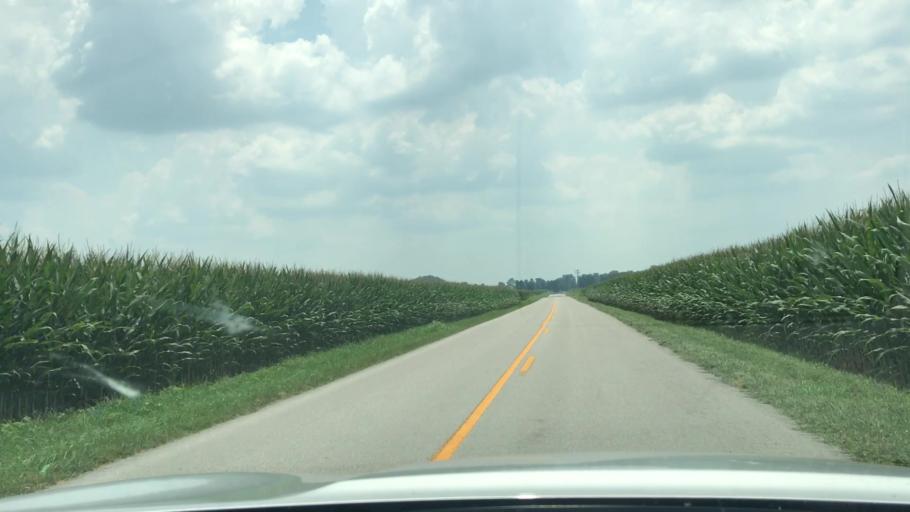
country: US
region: Kentucky
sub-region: Todd County
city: Elkton
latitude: 36.7517
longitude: -87.0965
